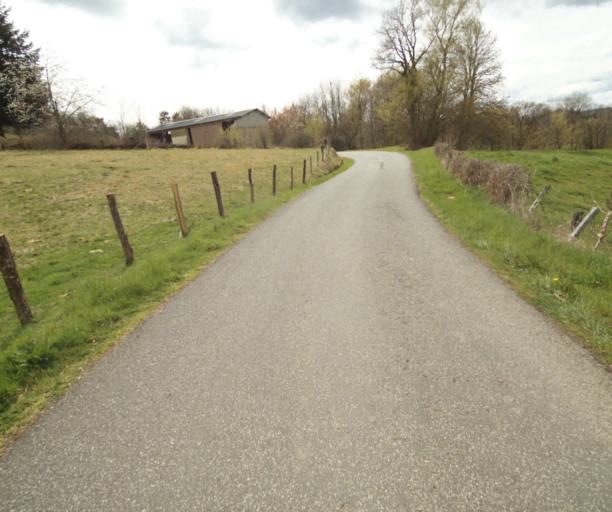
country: FR
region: Limousin
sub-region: Departement de la Correze
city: Laguenne
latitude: 45.2182
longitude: 1.8670
